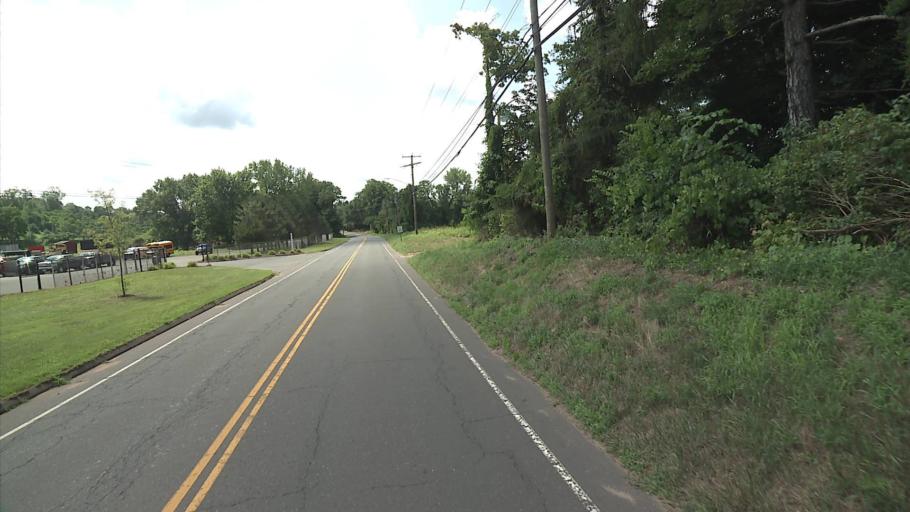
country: US
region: Connecticut
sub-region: Middlesex County
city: Cromwell
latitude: 41.6061
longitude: -72.6033
